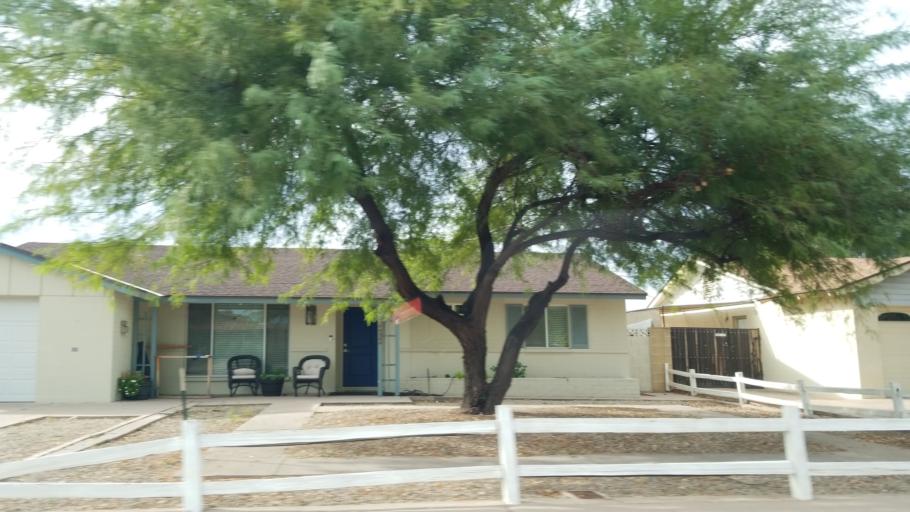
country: US
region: Arizona
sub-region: Maricopa County
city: Scottsdale
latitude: 33.4731
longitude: -111.9020
